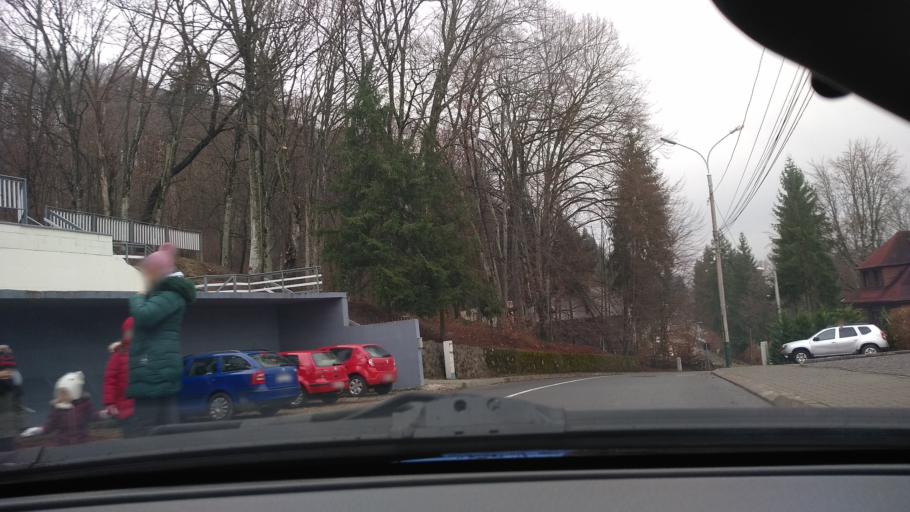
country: RO
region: Mures
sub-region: Oras Sovata
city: Sovata
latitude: 46.5996
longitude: 25.0871
